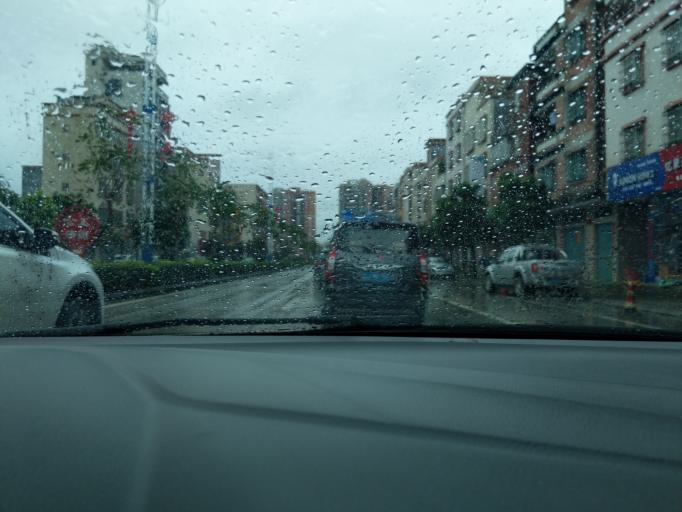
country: CN
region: Guangdong
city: Pingshi
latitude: 22.2002
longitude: 112.3306
